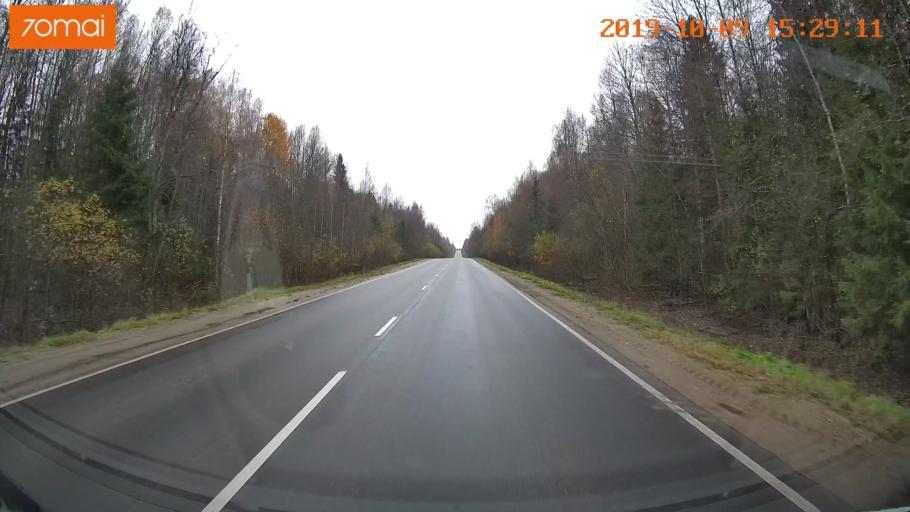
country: RU
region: Kostroma
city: Susanino
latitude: 57.9943
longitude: 41.3470
